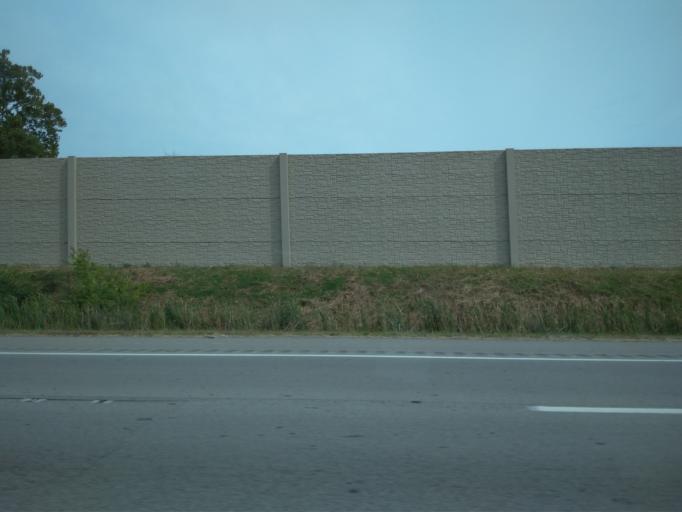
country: US
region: Kentucky
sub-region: Jefferson County
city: Hurstbourne Acres
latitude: 38.2267
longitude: -85.5886
